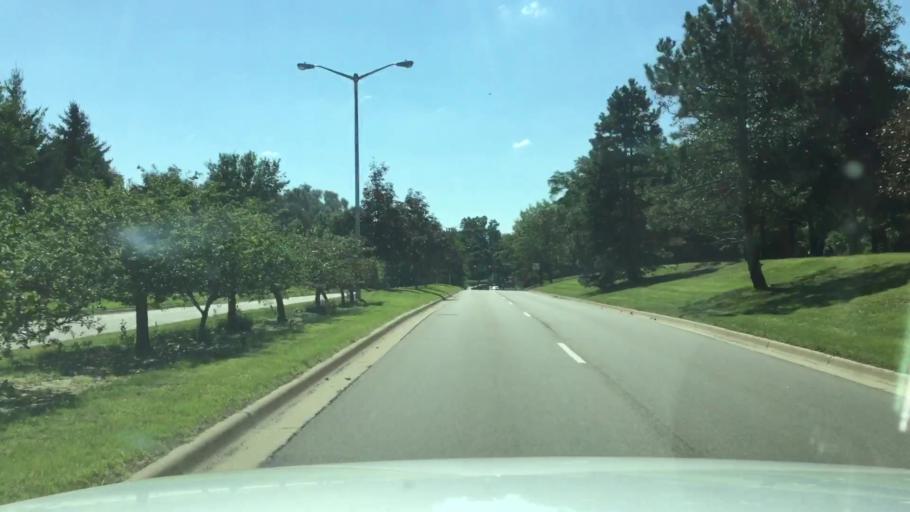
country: US
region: Michigan
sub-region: Kalamazoo County
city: Portage
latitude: 42.2176
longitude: -85.6032
